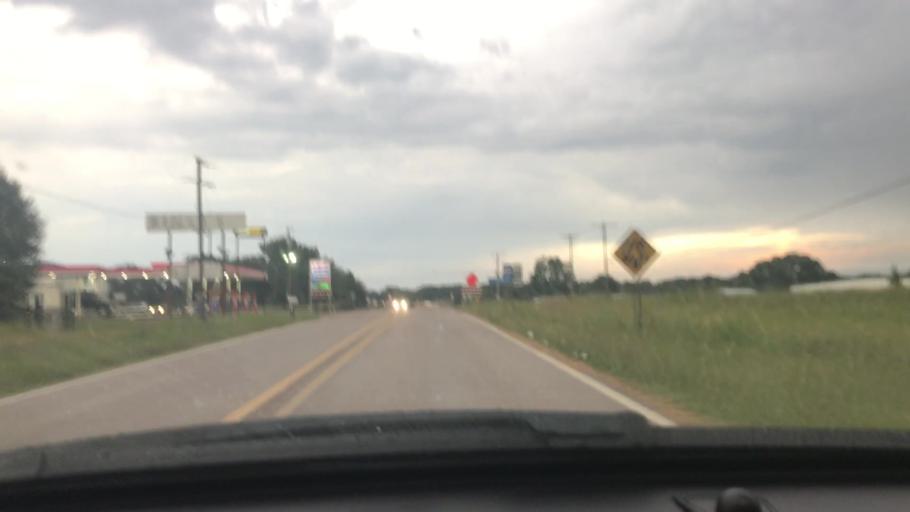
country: US
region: Mississippi
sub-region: Pike County
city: Summit
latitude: 31.2899
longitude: -90.4843
